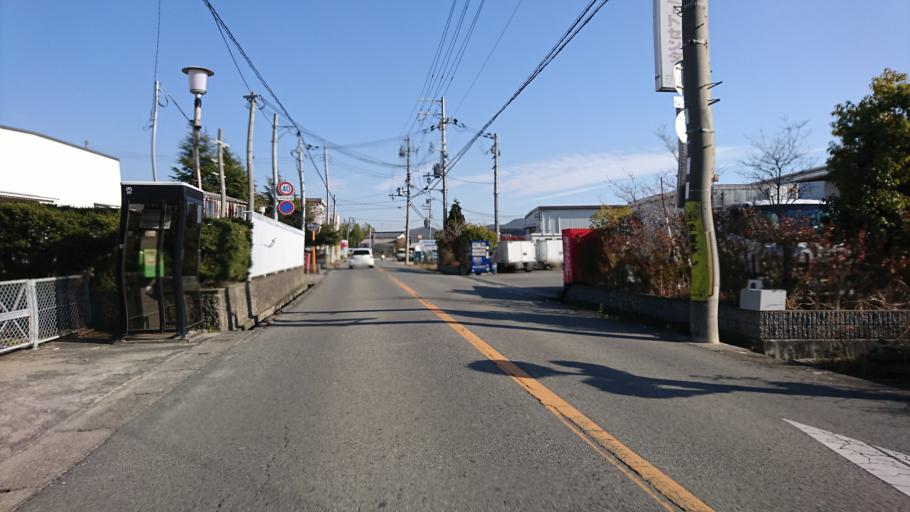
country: JP
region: Hyogo
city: Kakogawacho-honmachi
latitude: 34.8165
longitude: 134.8241
